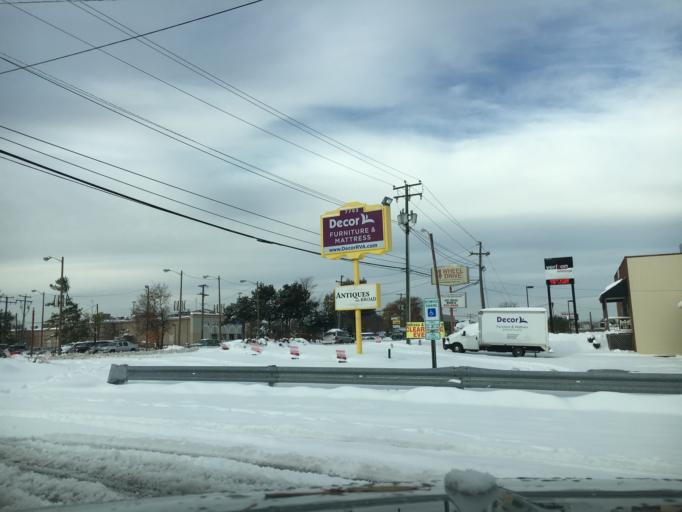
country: US
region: Virginia
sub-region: Henrico County
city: Laurel
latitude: 37.6203
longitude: -77.5242
